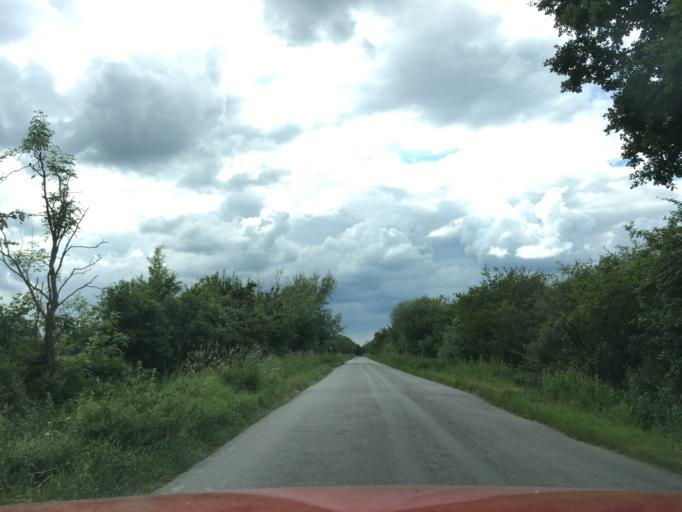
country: GB
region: England
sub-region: Wiltshire
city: Leigh
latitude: 51.6390
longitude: -1.9166
